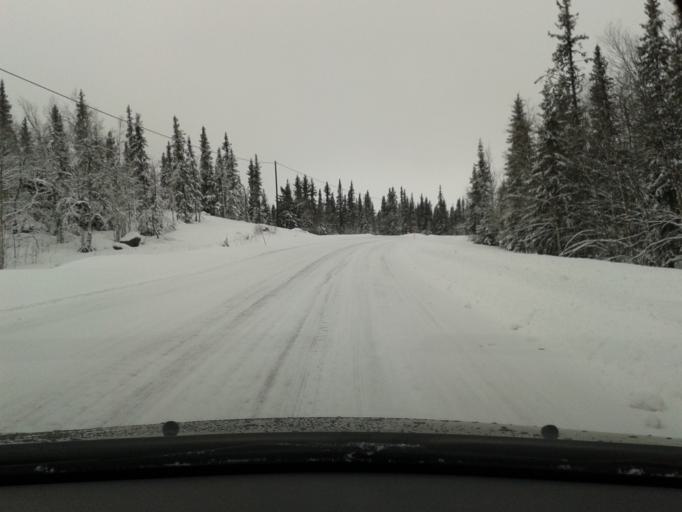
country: SE
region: Vaesterbotten
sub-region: Vilhelmina Kommun
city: Sjoberg
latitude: 65.1823
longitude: 15.8877
